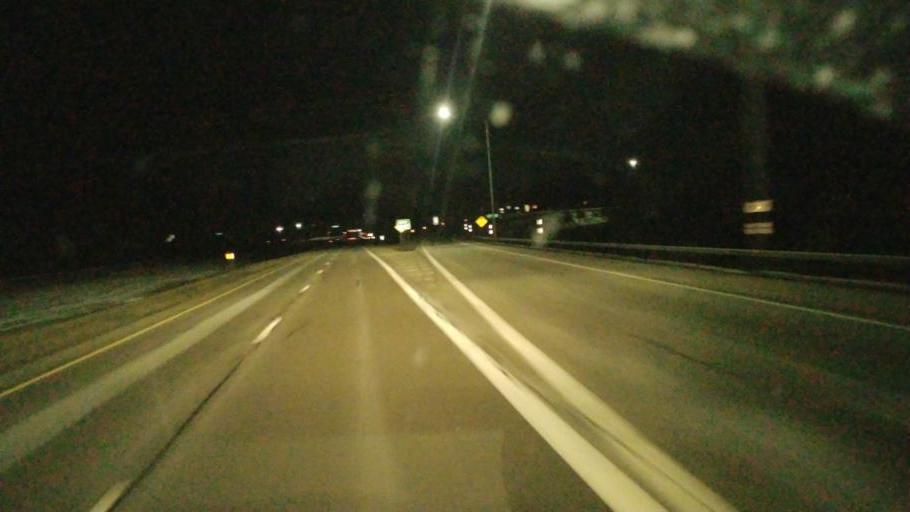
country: US
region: New York
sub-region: Cattaraugus County
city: Allegany
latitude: 42.1029
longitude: -78.5036
